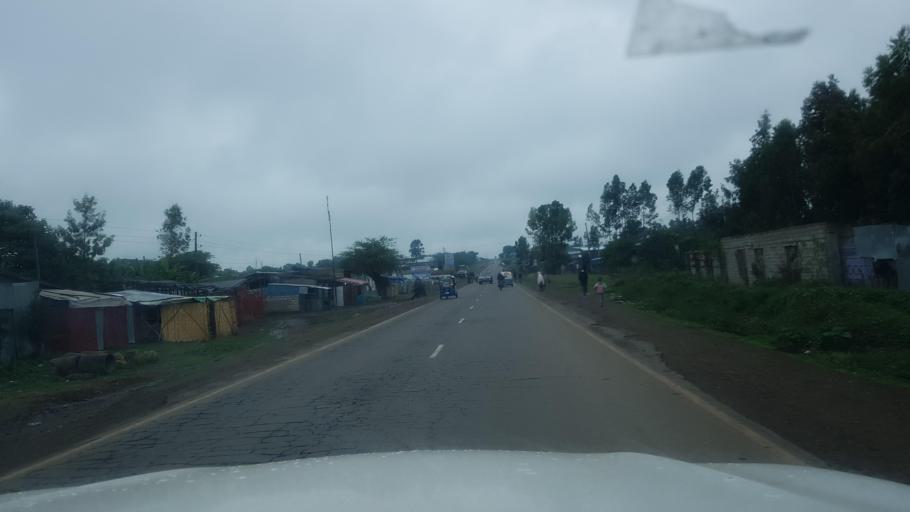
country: ET
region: Oromiya
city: Shashemene
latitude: 7.3725
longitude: 38.6715
